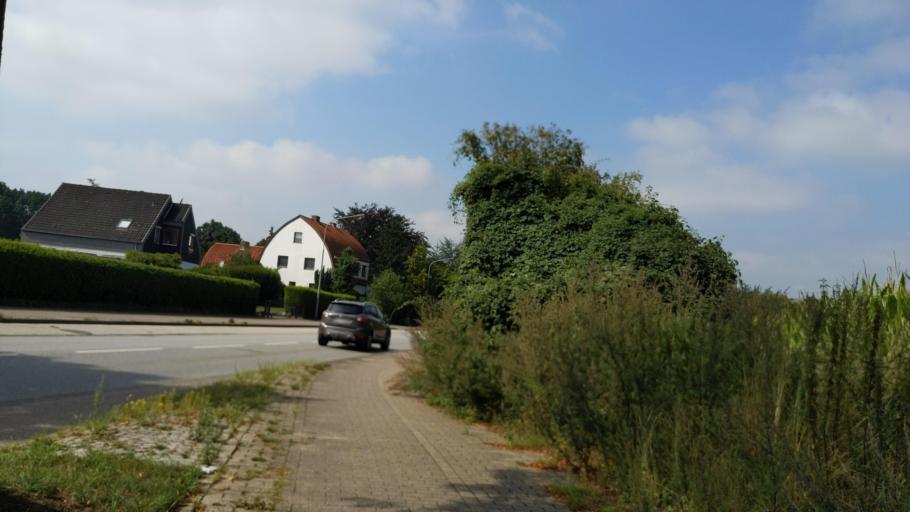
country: DE
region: Schleswig-Holstein
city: Stockelsdorf
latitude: 53.8695
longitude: 10.6293
